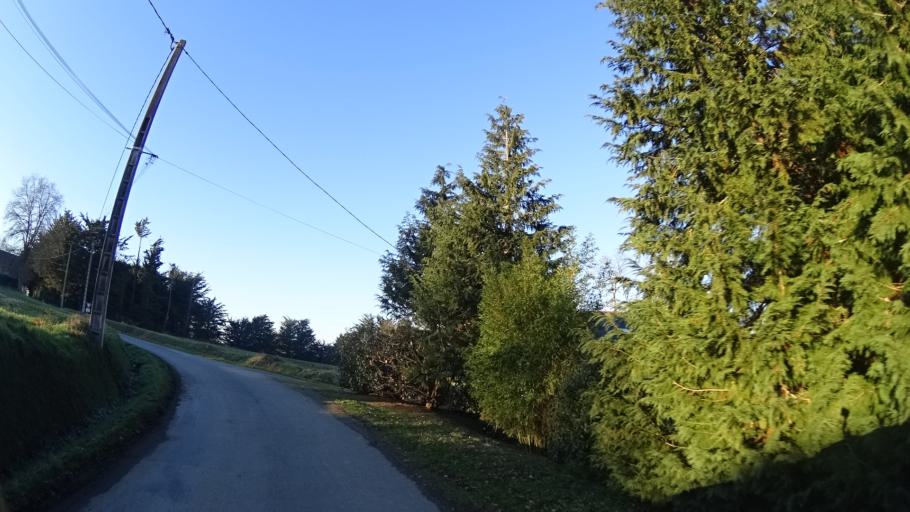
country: FR
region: Brittany
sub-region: Departement du Morbihan
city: Saint-Perreux
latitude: 47.6586
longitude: -2.1192
